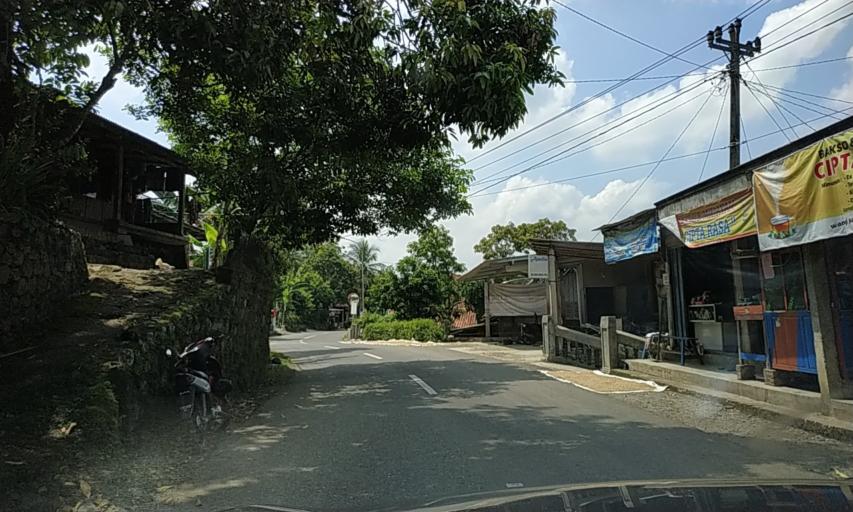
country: ID
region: Central Java
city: Gombong
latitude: -7.6285
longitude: 109.7187
